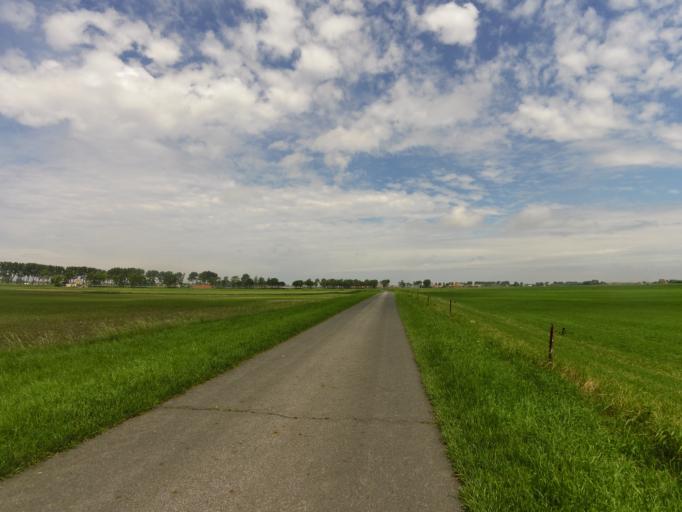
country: BE
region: Flanders
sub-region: Provincie West-Vlaanderen
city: Nieuwpoort
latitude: 51.1391
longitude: 2.7851
